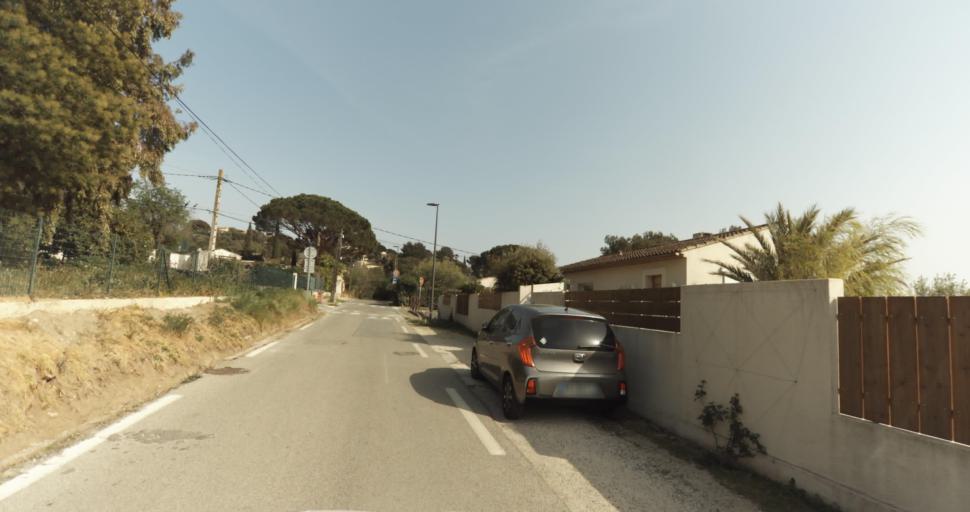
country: FR
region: Provence-Alpes-Cote d'Azur
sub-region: Departement du Var
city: Bormes-les-Mimosas
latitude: 43.1448
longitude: 6.3285
